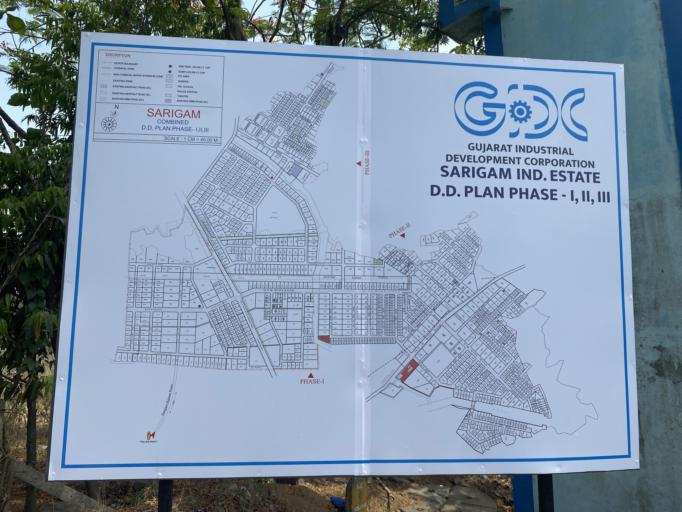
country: IN
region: Gujarat
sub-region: Valsad
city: Vapi
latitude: 20.2816
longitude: 72.8727
